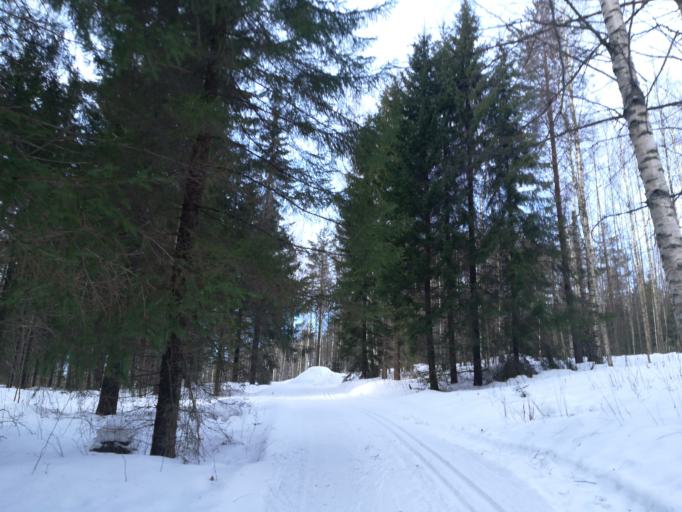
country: FI
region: Southern Savonia
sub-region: Savonlinna
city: Savonlinna
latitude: 61.8069
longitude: 29.0555
